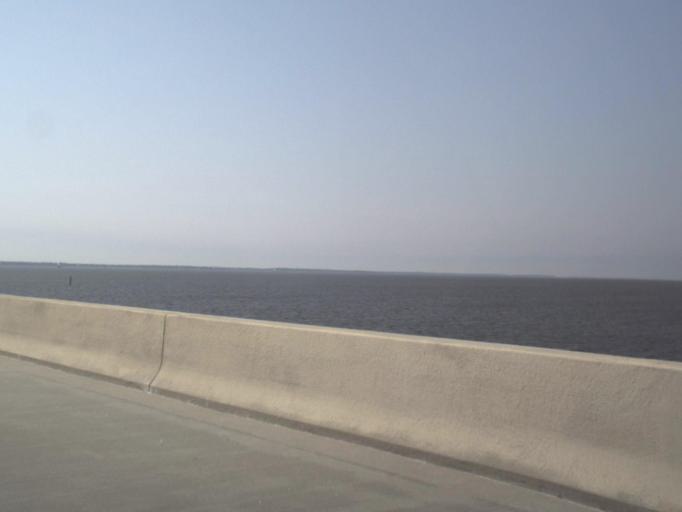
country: US
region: Florida
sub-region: Franklin County
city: Eastpoint
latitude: 29.6978
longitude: -84.8897
